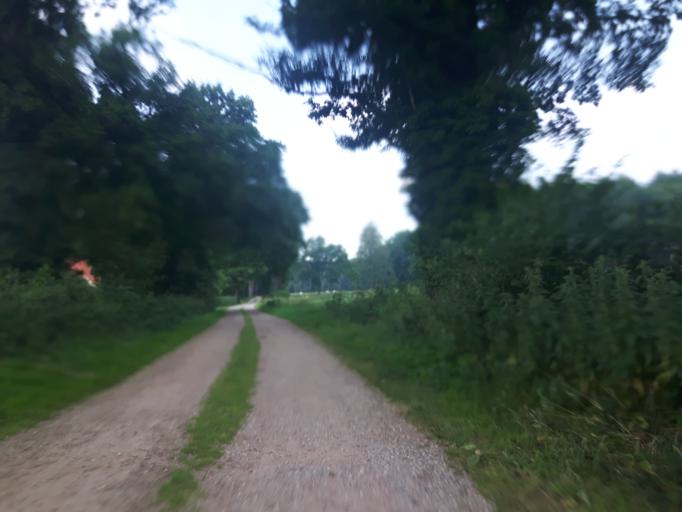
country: NL
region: Overijssel
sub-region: Gemeente Hof van Twente
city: Delden
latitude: 52.2897
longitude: 6.7140
